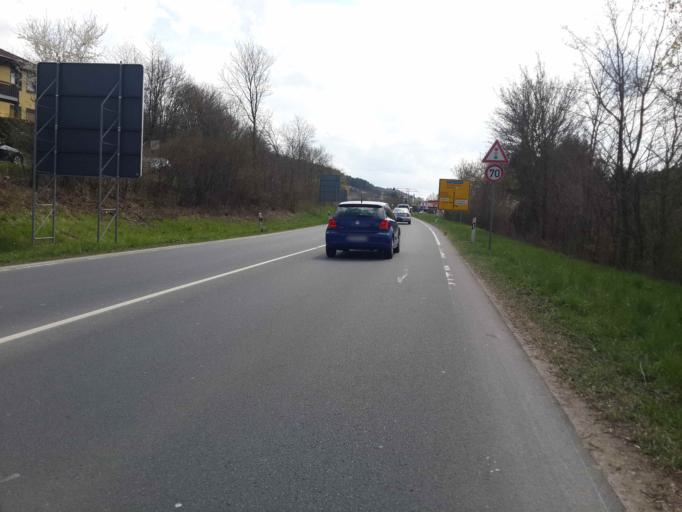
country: DE
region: Baden-Wuerttemberg
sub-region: Regierungsbezirk Stuttgart
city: Bad Mergentheim
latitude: 49.4783
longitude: 9.7706
